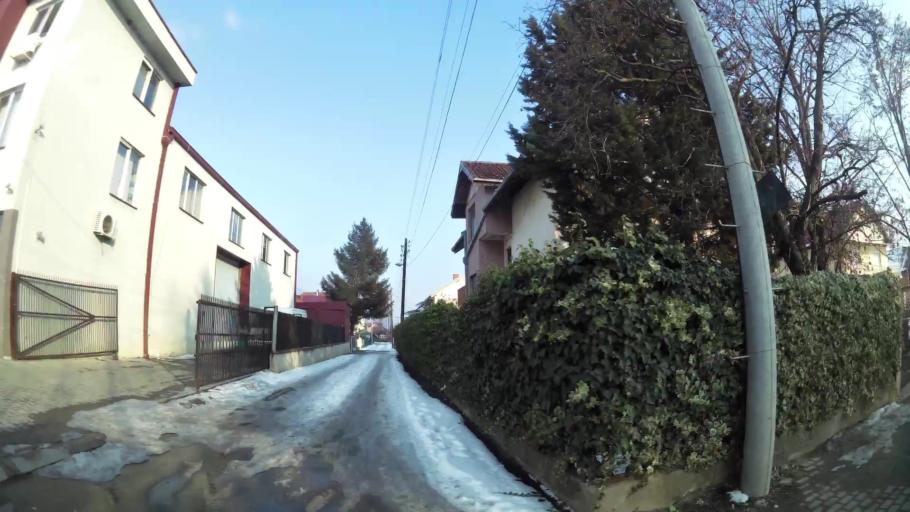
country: MK
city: Creshevo
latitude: 42.0295
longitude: 21.5125
